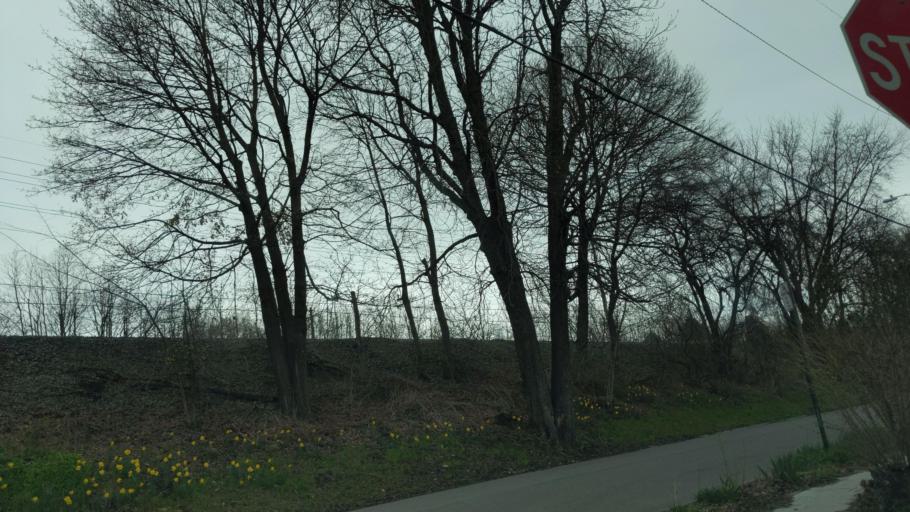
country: US
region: Ohio
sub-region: Cuyahoga County
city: Brooklyn
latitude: 41.4833
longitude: -81.7473
